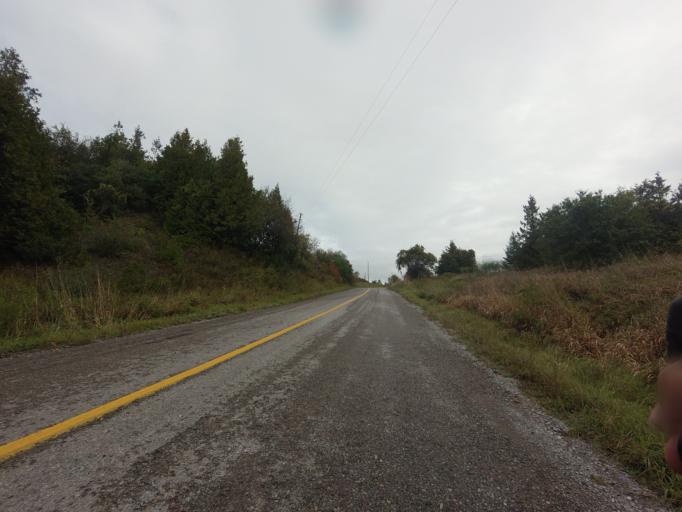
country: CA
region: Ontario
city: Cobourg
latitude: 43.9081
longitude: -78.4574
